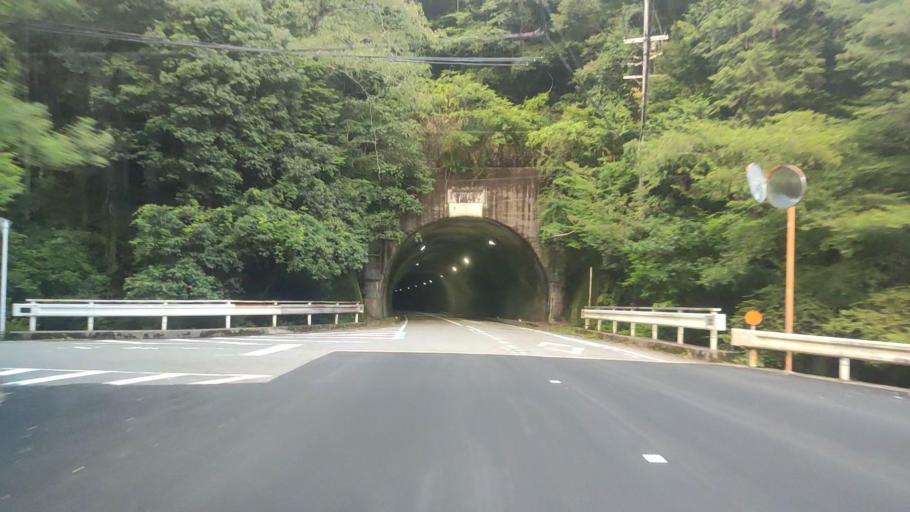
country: JP
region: Wakayama
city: Shingu
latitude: 33.8067
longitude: 135.7133
